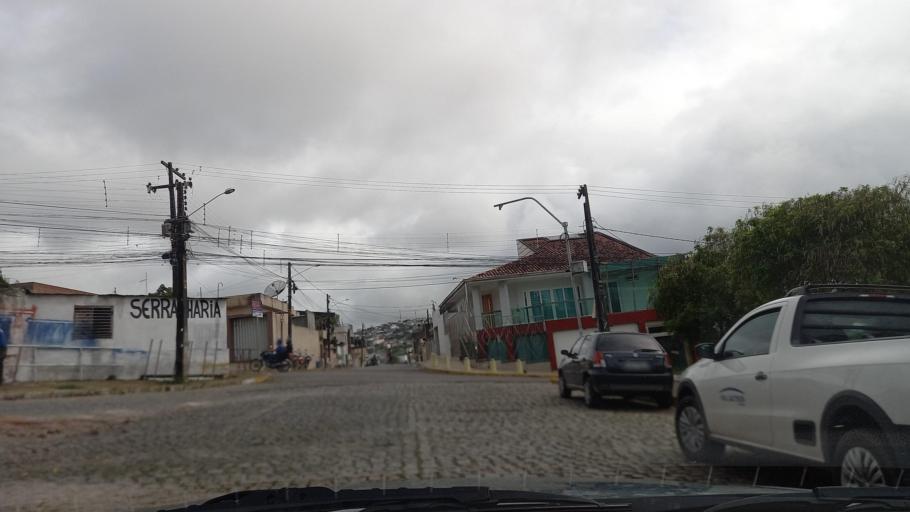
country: BR
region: Pernambuco
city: Garanhuns
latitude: -8.8996
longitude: -36.4926
